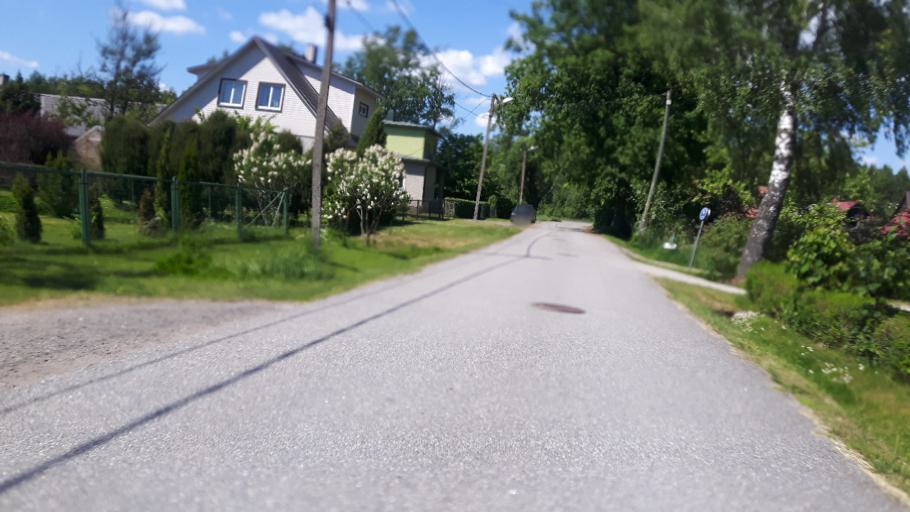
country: EE
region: Paernumaa
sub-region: Sindi linn
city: Sindi
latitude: 58.4132
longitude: 24.6736
